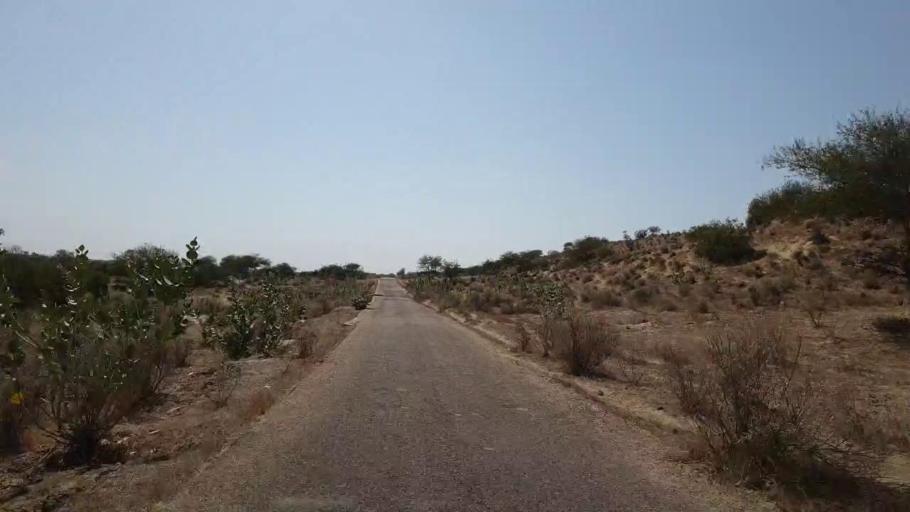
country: PK
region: Sindh
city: Umarkot
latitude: 25.2297
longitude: 69.8919
